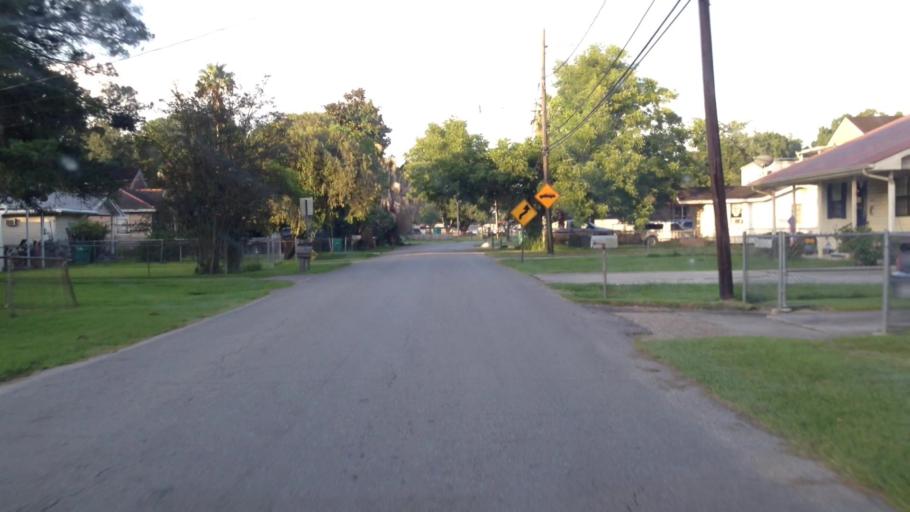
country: US
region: Louisiana
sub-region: Jefferson Parish
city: Bridge City
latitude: 29.9339
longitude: -90.1581
